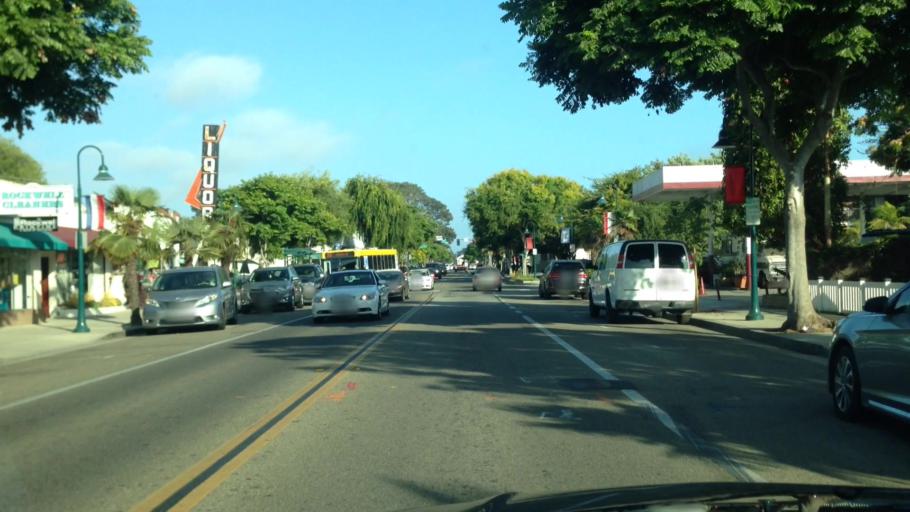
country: US
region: California
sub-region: Santa Barbara County
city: Carpinteria
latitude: 34.4003
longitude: -119.5200
